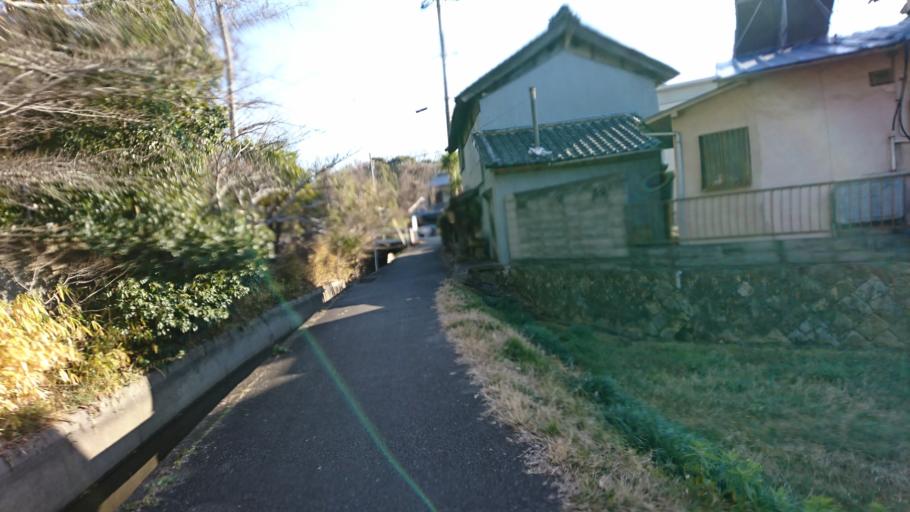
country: JP
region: Hyogo
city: Kakogawacho-honmachi
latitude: 34.7787
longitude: 134.8597
